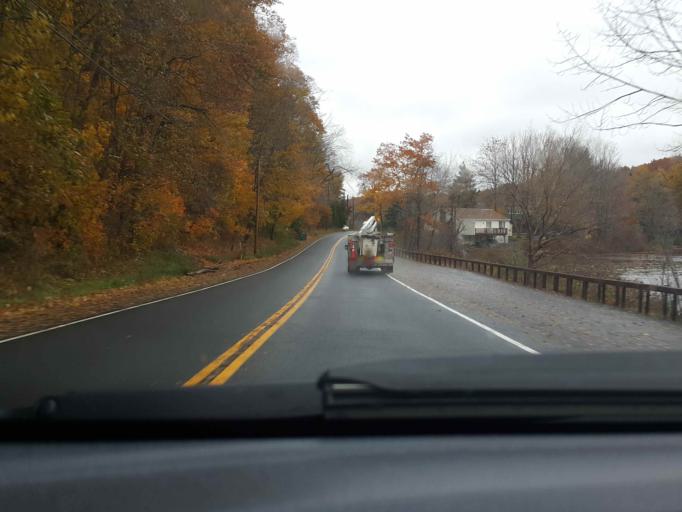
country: US
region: Connecticut
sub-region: Middlesex County
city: Durham
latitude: 41.3961
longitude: -72.6980
